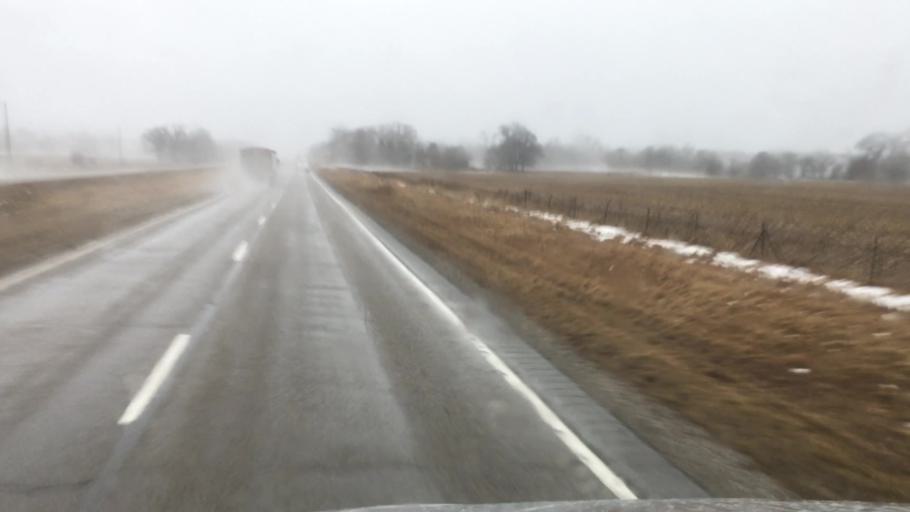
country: US
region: Indiana
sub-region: Newton County
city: Roselawn
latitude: 41.1147
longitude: -87.4489
